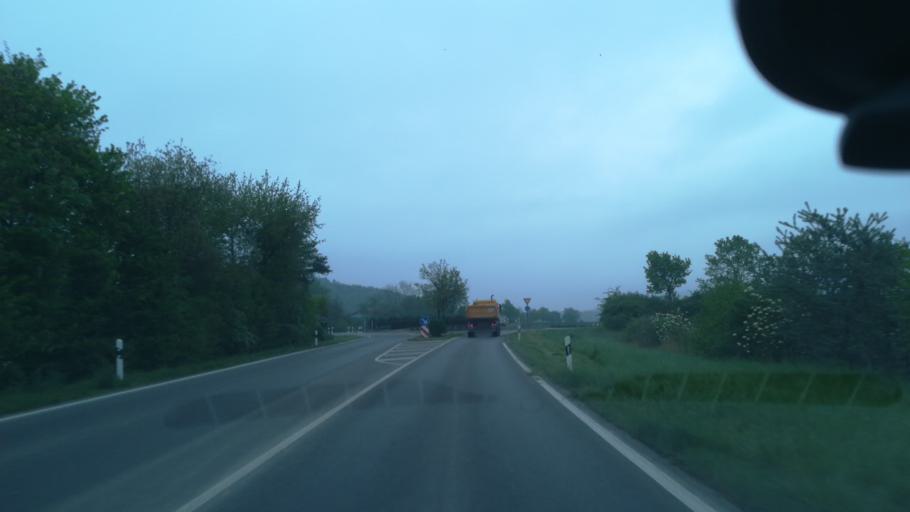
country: DE
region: Baden-Wuerttemberg
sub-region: Freiburg Region
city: Steisslingen
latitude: 47.7828
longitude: 8.9158
